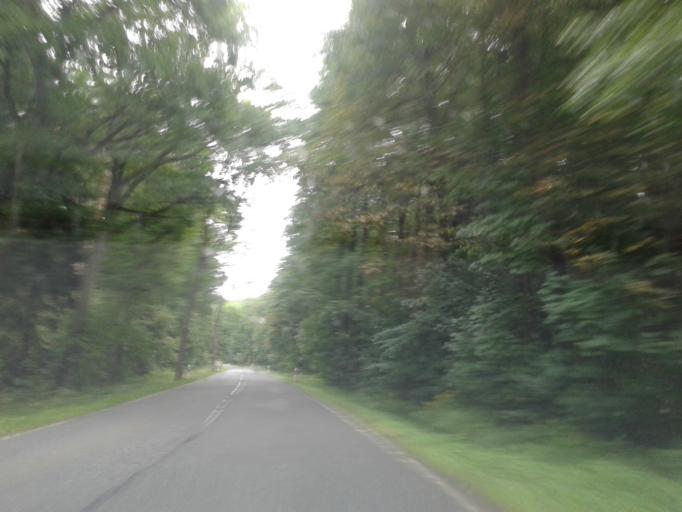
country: DE
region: Saxony
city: Niederschona
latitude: 50.9445
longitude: 13.4718
